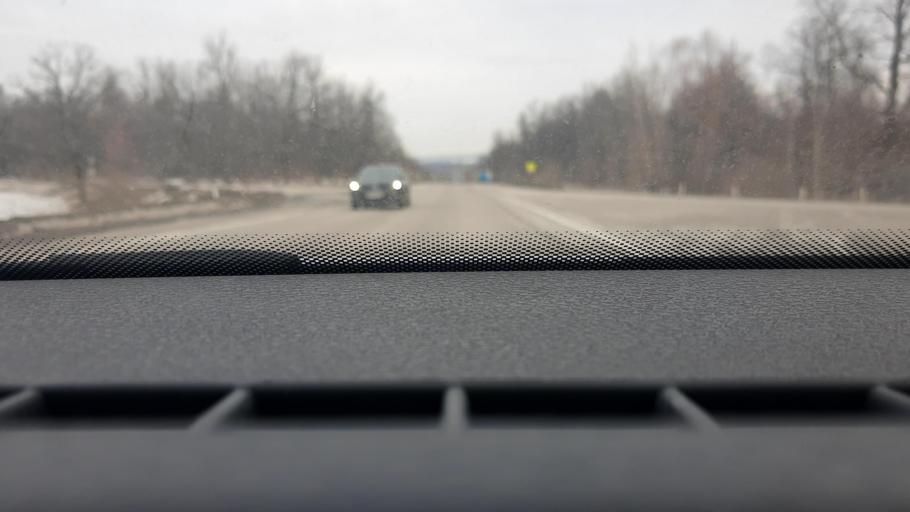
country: RU
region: Chelyabinsk
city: Asha
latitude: 54.9310
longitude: 57.2882
